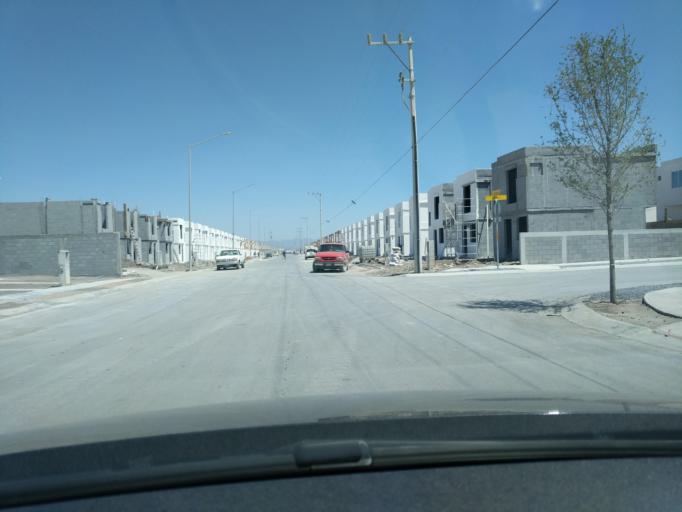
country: MX
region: Nuevo Leon
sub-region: Salinas Victoria
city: Emiliano Zapata
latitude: 25.9100
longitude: -100.2647
